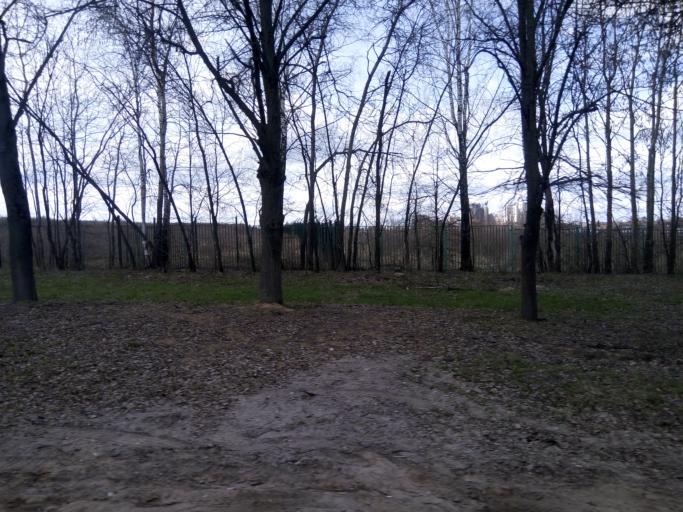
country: RU
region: Moskovskaya
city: Marfino
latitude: 55.6959
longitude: 37.3880
